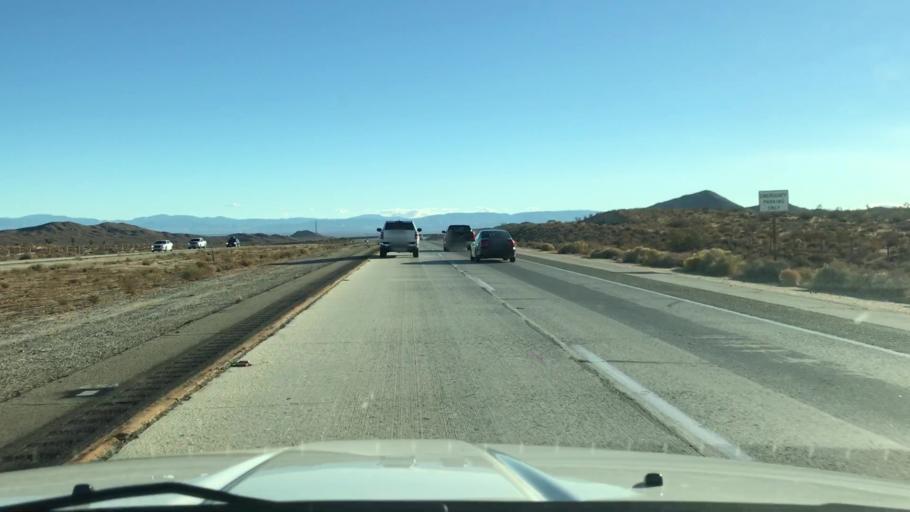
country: US
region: California
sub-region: Kern County
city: Rosamond
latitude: 34.9155
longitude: -118.1641
